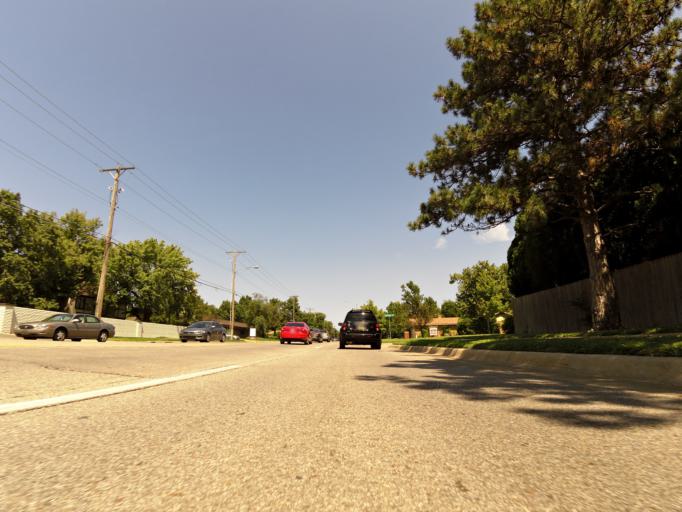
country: US
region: Kansas
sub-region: Sedgwick County
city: Bellaire
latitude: 37.6962
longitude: -97.2621
